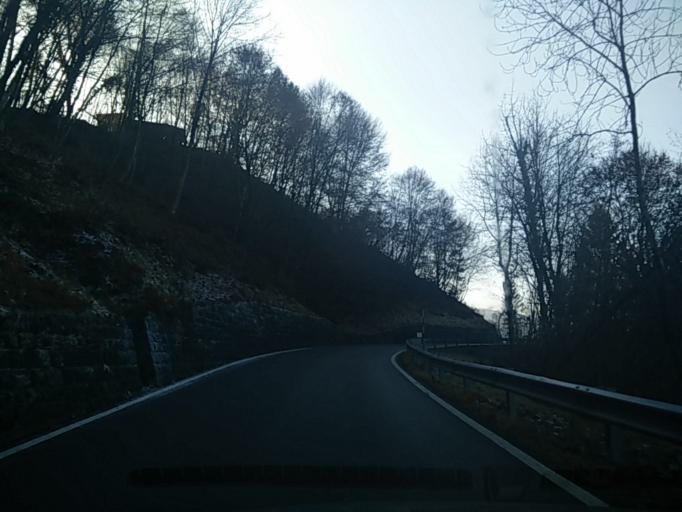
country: IT
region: Veneto
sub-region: Provincia di Belluno
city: Trichiana
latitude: 46.0357
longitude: 12.1660
